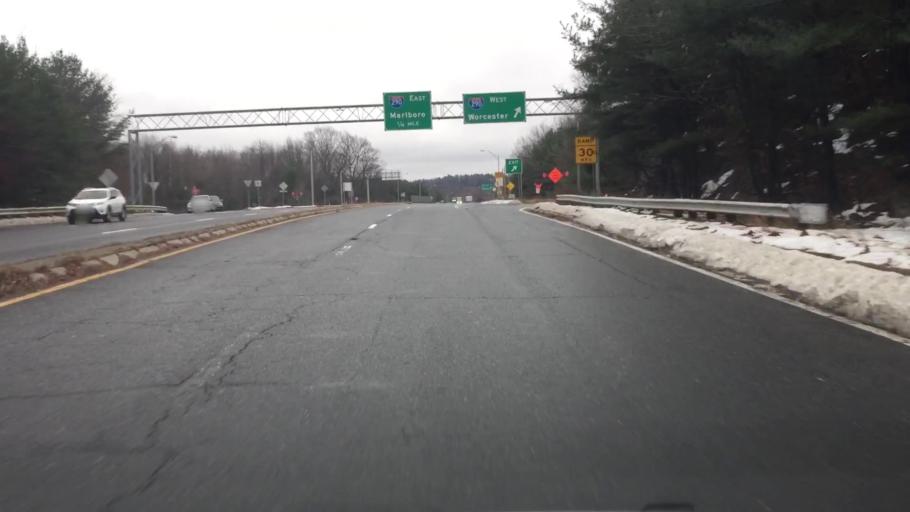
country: US
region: Massachusetts
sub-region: Worcester County
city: Shrewsbury
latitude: 42.3241
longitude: -71.7203
